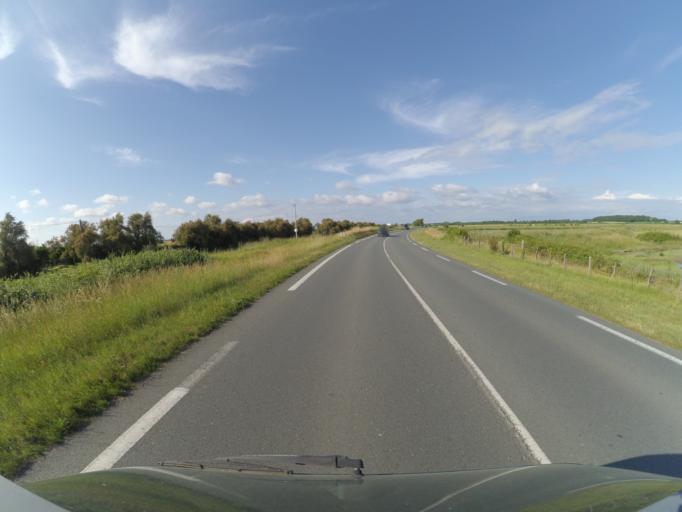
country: FR
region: Poitou-Charentes
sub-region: Departement de la Charente-Maritime
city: Le Gua
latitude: 45.7144
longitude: -0.9727
